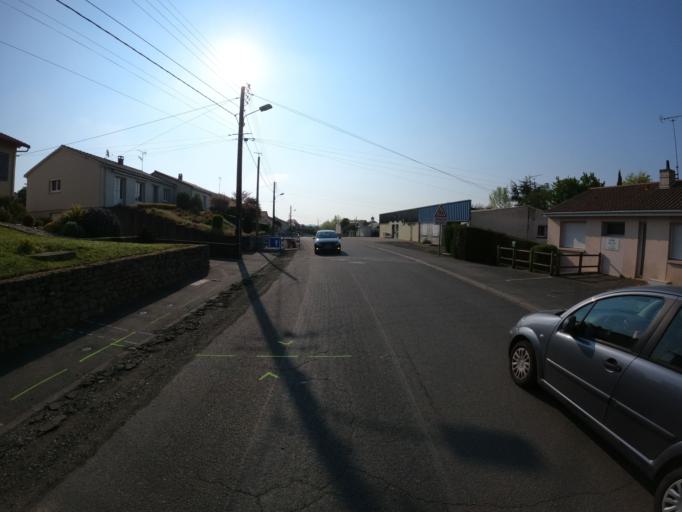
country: FR
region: Pays de la Loire
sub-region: Departement de Maine-et-Loire
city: La Seguiniere
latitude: 47.0636
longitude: -0.9428
